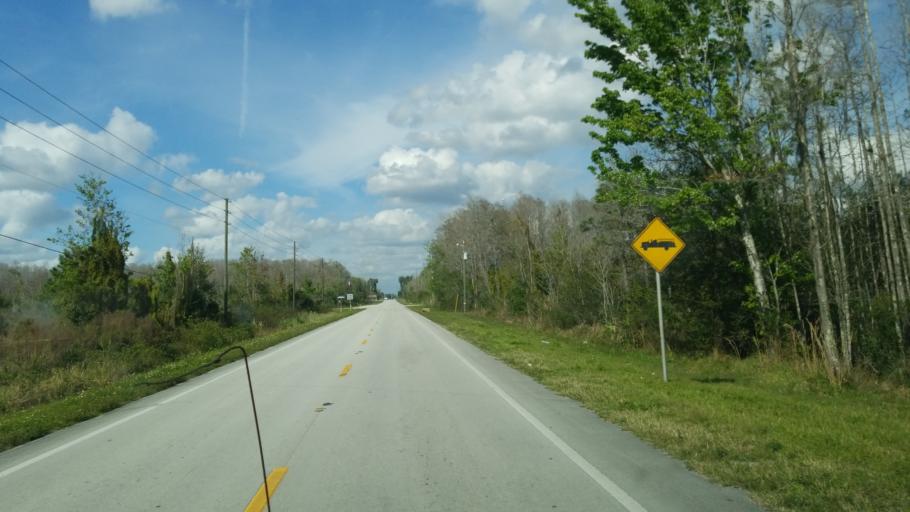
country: US
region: Florida
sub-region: Osceola County
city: Saint Cloud
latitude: 28.1294
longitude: -81.0763
